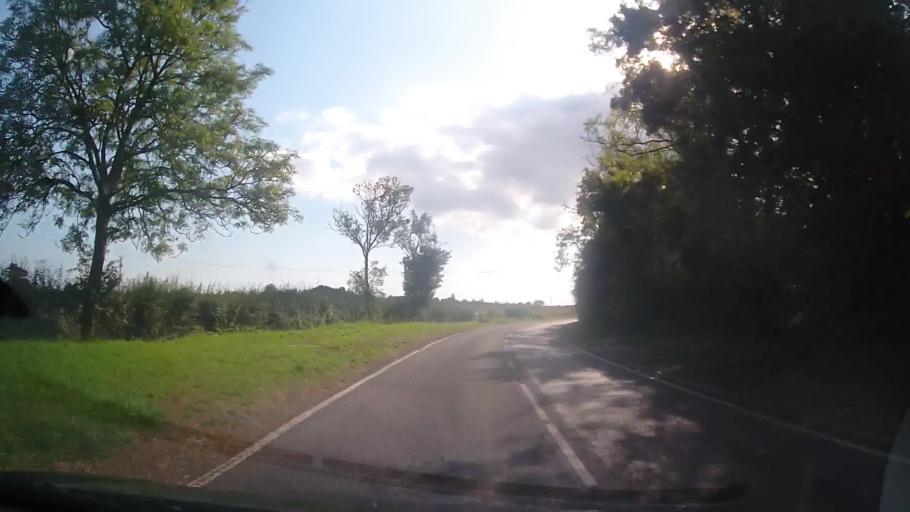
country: GB
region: England
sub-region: Kent
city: Hythe
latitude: 51.0978
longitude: 1.0656
